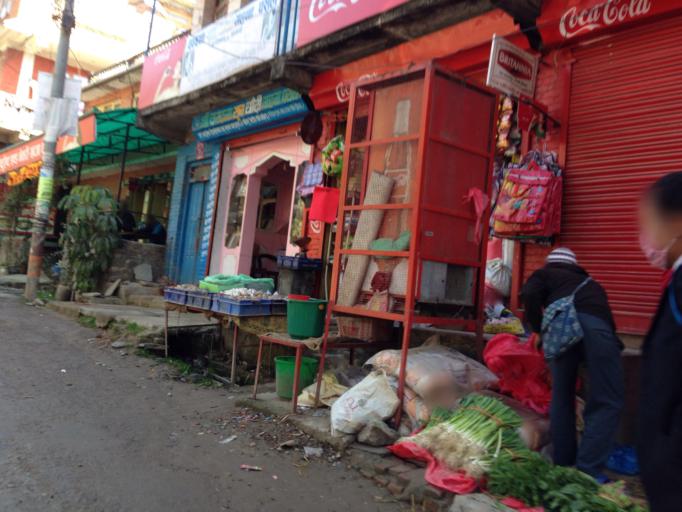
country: NP
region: Central Region
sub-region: Bagmati Zone
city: Kathmandu
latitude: 27.7777
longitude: 85.3627
